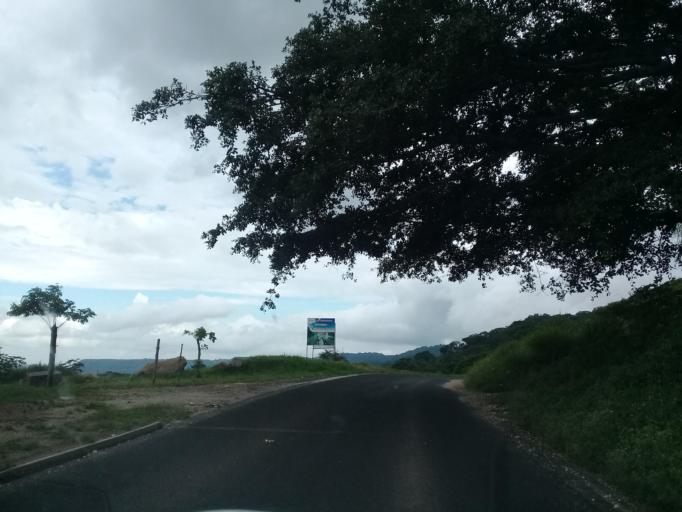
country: MX
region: Veracruz
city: El Castillo
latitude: 19.5641
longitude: -96.8446
